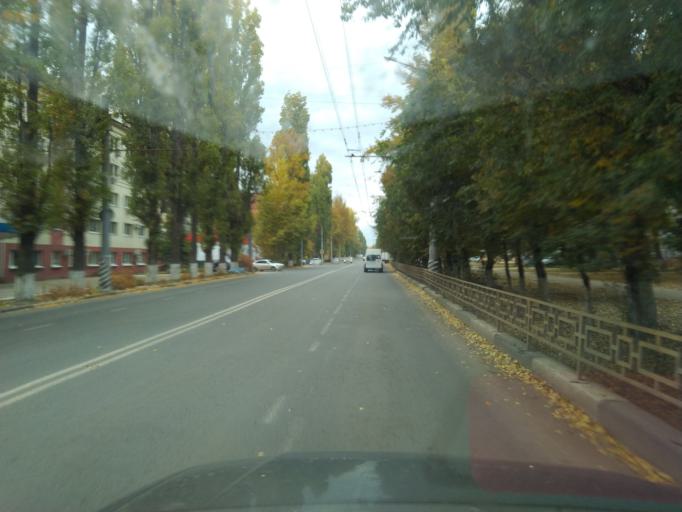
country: RU
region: Saratov
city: Engel's
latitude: 51.4743
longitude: 46.1321
